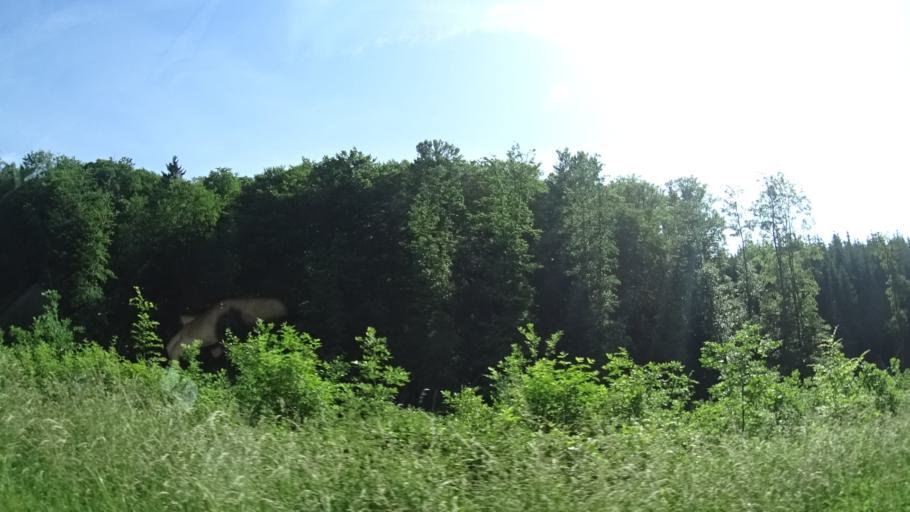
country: DE
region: Hesse
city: Beuern
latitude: 50.6472
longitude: 8.8323
